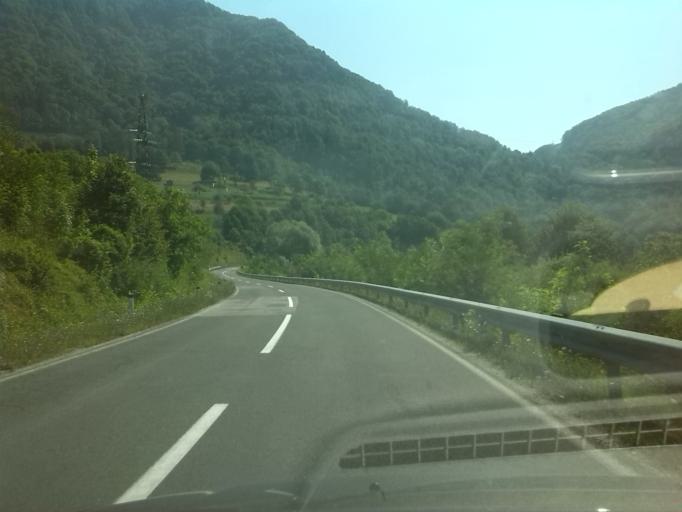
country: SI
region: Tolmin
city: Tolmin
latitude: 46.1703
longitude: 13.7492
